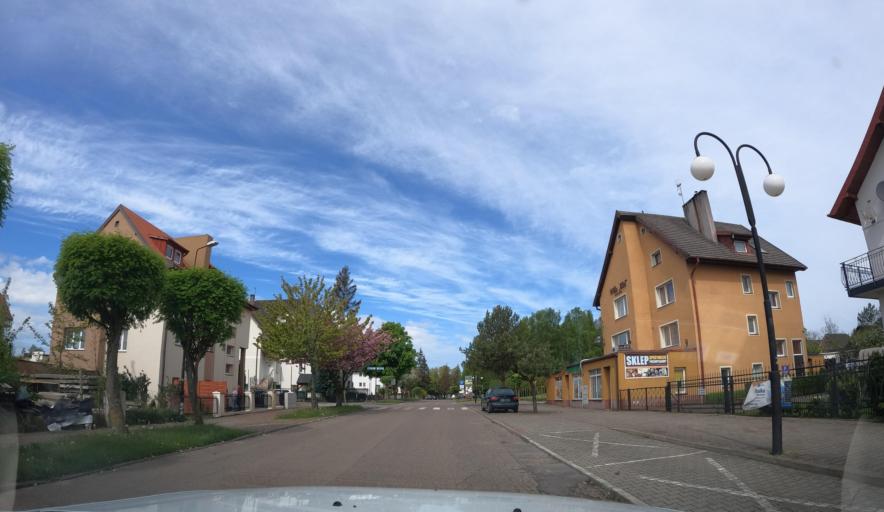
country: PL
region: West Pomeranian Voivodeship
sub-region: Powiat gryficki
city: Rewal
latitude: 54.0820
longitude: 15.0227
